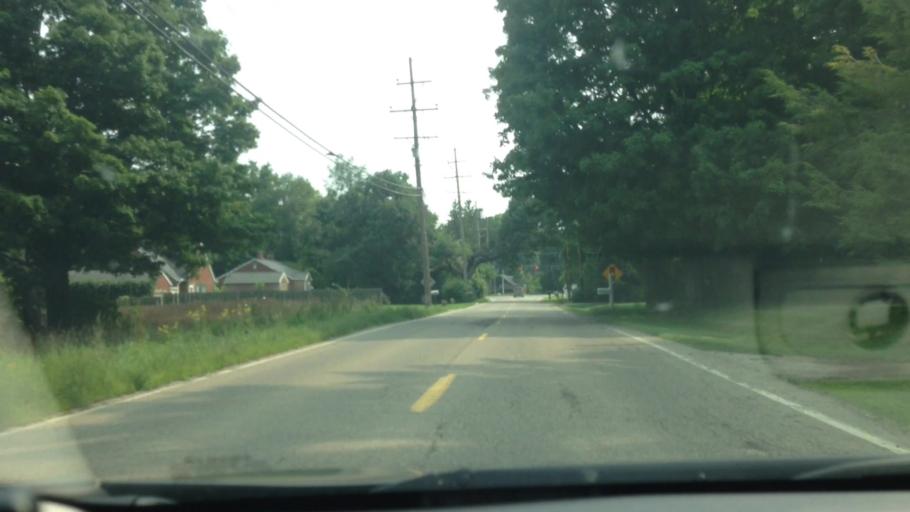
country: US
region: Ohio
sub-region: Summit County
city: Fairlawn
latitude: 41.0854
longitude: -81.5904
